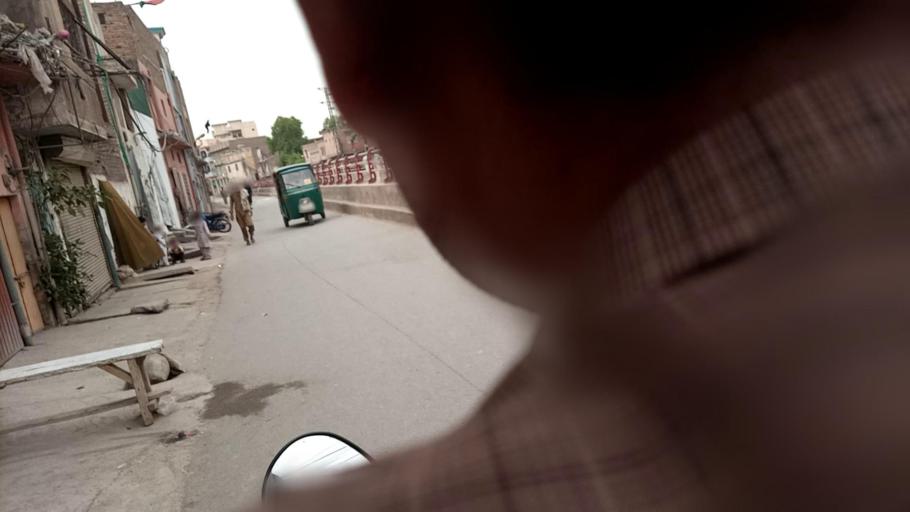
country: PK
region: Khyber Pakhtunkhwa
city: Peshawar
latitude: 34.0195
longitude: 71.5926
